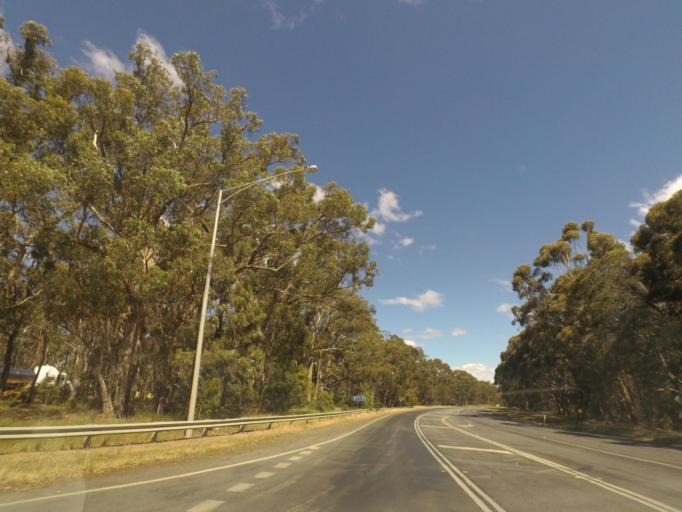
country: AU
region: Victoria
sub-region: Hume
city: Sunbury
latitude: -37.4186
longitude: 144.5518
